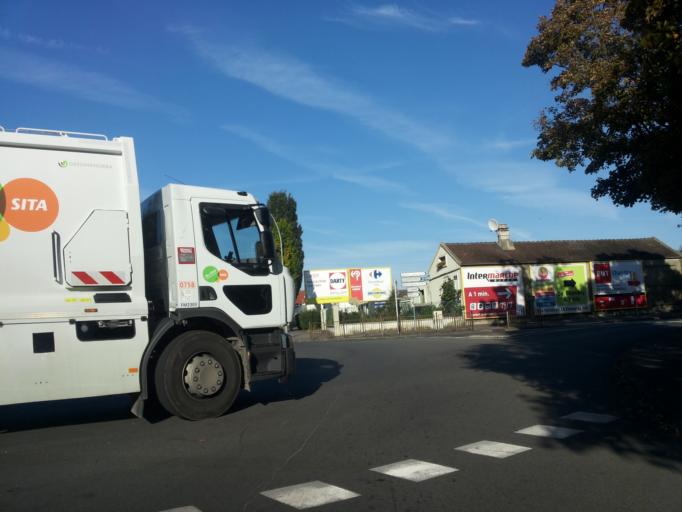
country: FR
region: Picardie
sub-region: Departement de l'Aisne
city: Laon
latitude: 49.5688
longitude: 3.6474
